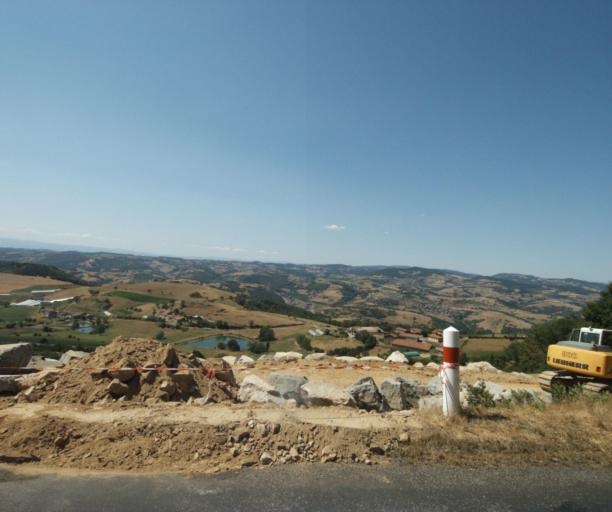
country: FR
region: Rhone-Alpes
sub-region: Departement du Rhone
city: Courzieu
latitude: 45.7222
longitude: 4.5513
